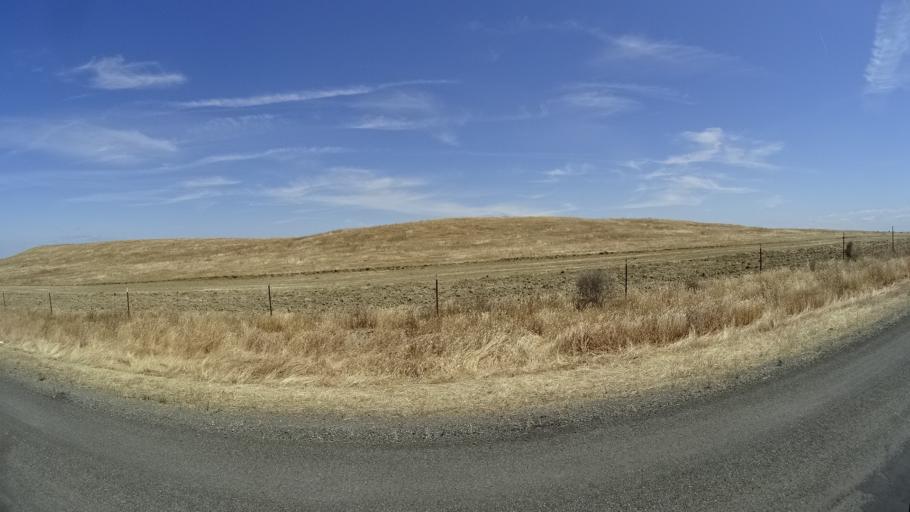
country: US
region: California
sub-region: Kings County
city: Kettleman City
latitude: 35.8278
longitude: -119.9115
